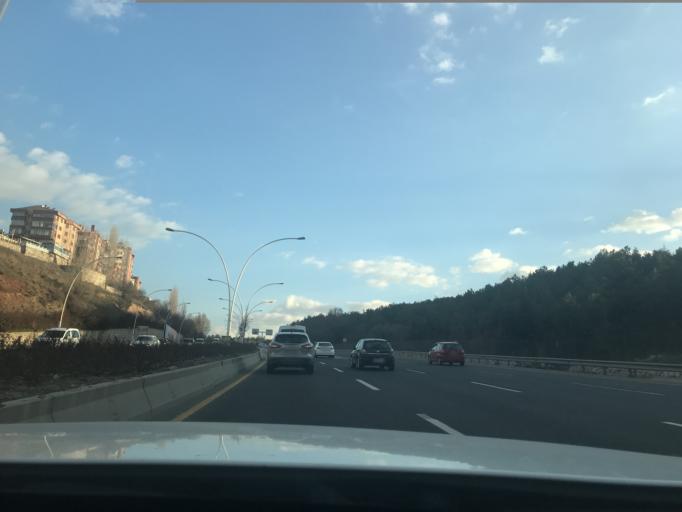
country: TR
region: Ankara
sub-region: Goelbasi
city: Golbasi
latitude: 39.8545
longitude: 32.8091
